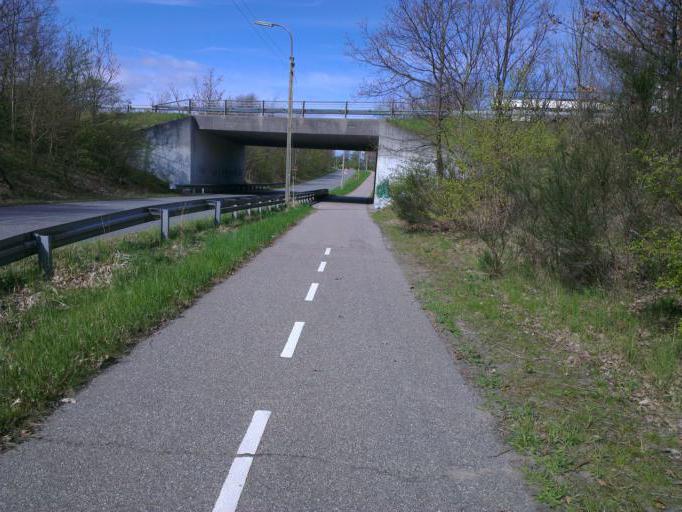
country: DK
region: Capital Region
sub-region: Frederikssund Kommune
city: Jaegerspris
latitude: 55.8221
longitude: 12.0067
